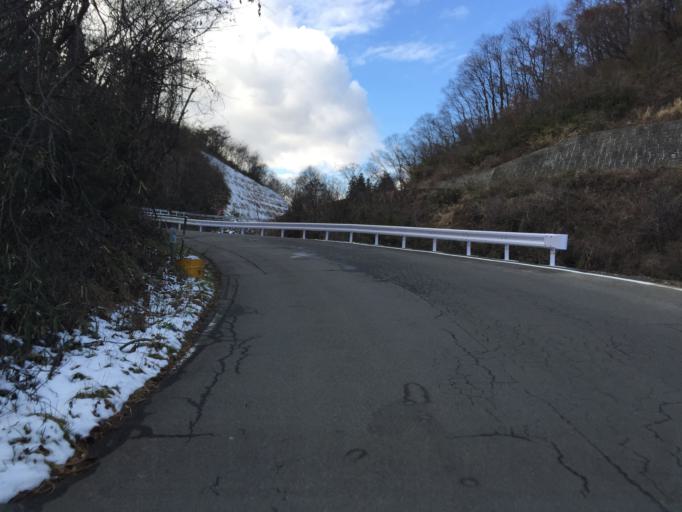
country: JP
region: Fukushima
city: Nihommatsu
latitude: 37.6711
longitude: 140.3761
